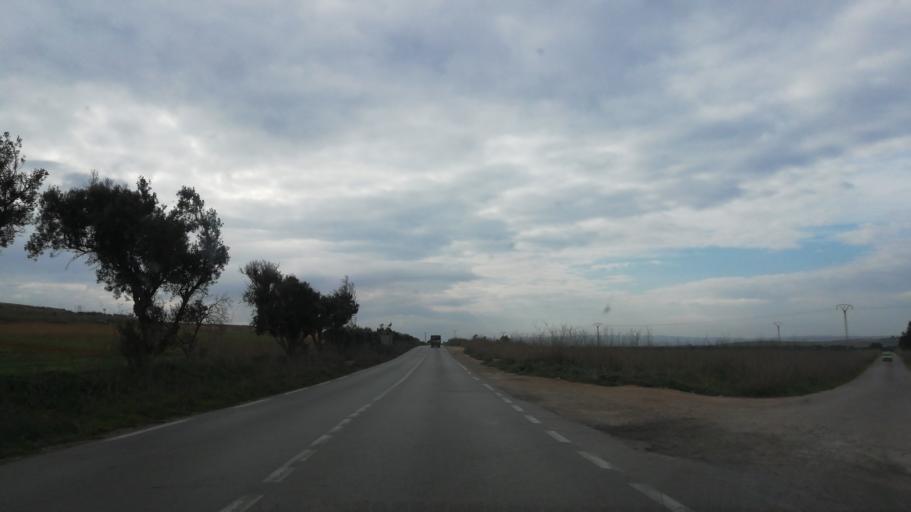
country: DZ
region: Oran
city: Ain el Bya
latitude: 35.7517
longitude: -0.3521
